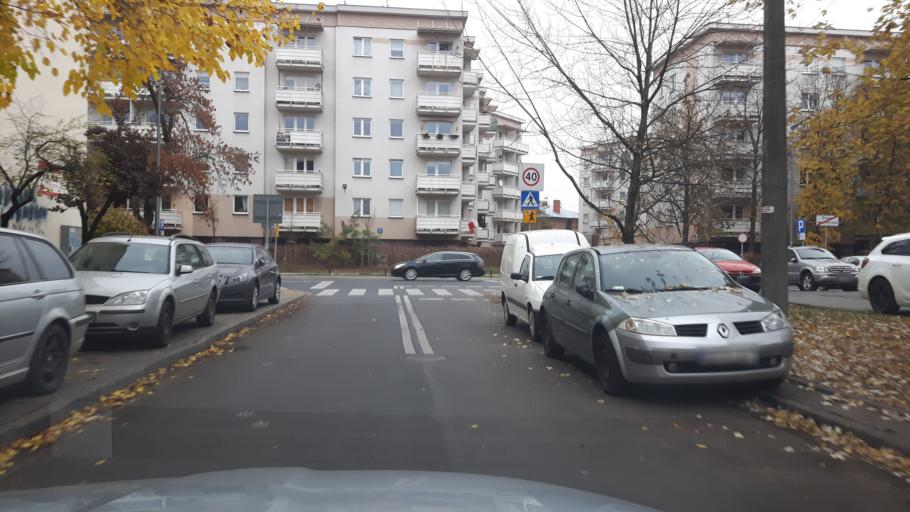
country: PL
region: Masovian Voivodeship
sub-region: Warszawa
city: Praga Polnoc
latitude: 52.2616
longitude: 21.0354
